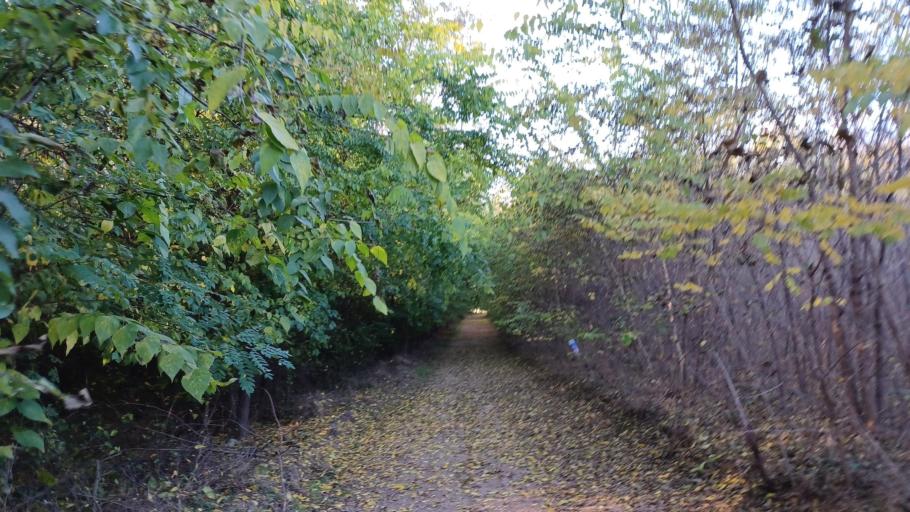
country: HU
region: Tolna
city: Tengelic
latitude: 46.5402
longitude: 18.6875
